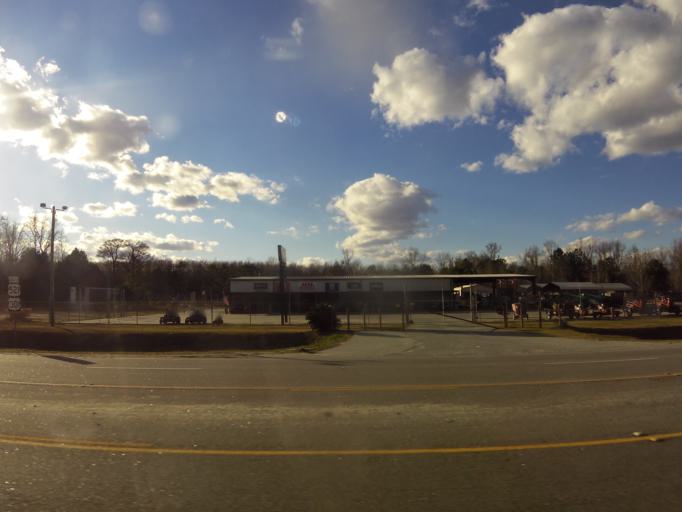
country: US
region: South Carolina
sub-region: Clarendon County
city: Manning
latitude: 33.7191
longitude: -80.1959
